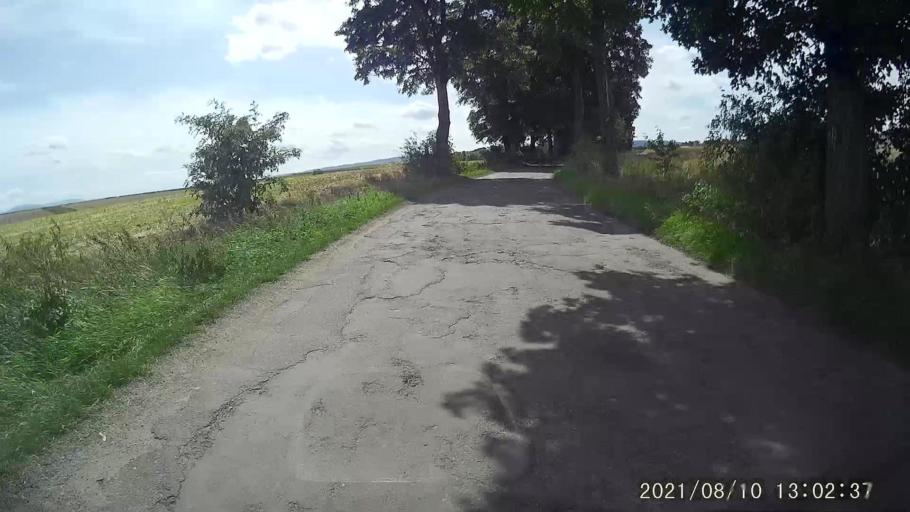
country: PL
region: Lower Silesian Voivodeship
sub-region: Powiat klodzki
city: Bozkow
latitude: 50.4657
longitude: 16.5589
